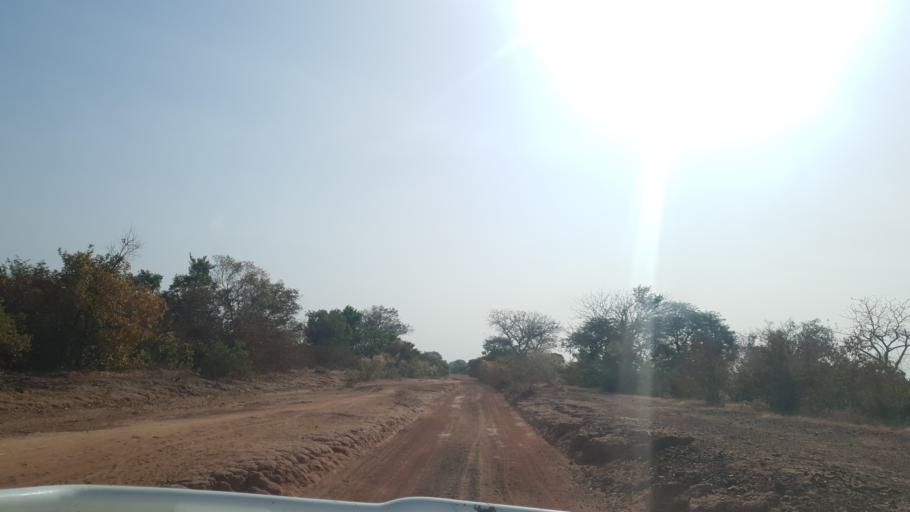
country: ML
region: Koulikoro
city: Dioila
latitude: 12.7100
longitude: -6.7850
